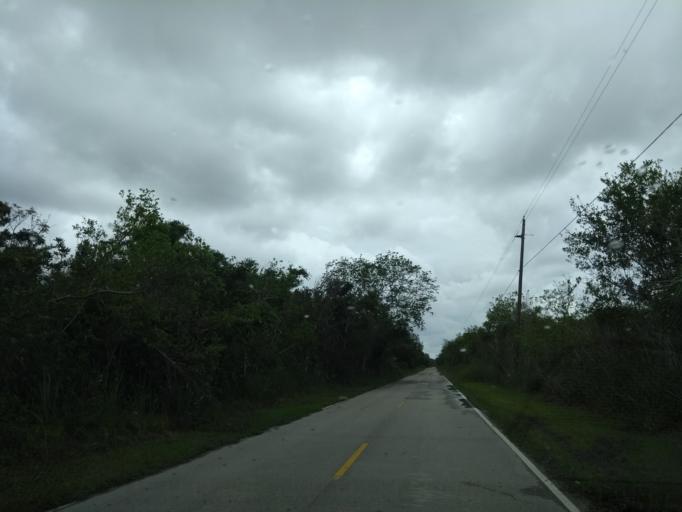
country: US
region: Florida
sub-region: Miami-Dade County
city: The Hammocks
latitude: 25.7604
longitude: -80.9235
